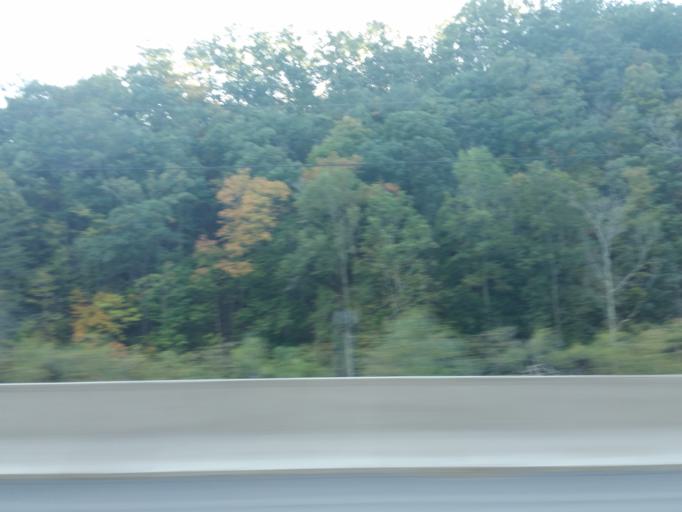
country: US
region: Tennessee
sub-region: Grainger County
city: Bean Station
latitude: 36.3491
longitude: -83.3375
